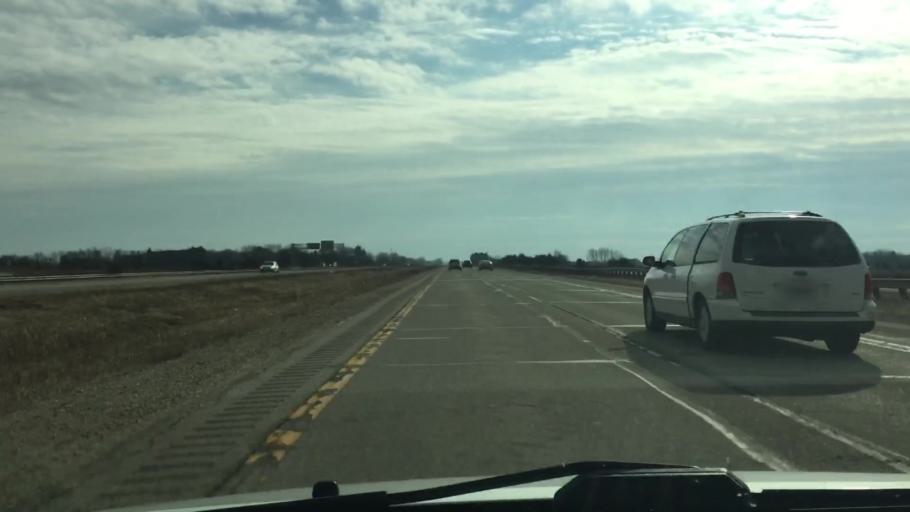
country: US
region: Wisconsin
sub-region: Walworth County
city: Elkhorn
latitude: 42.6692
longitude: -88.5182
